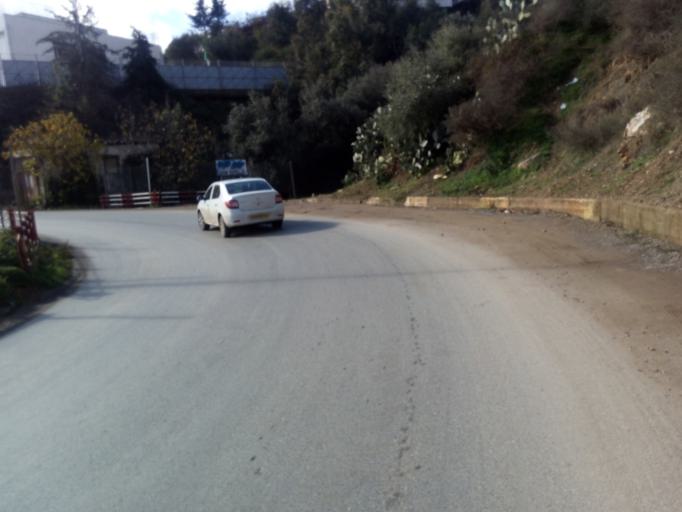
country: DZ
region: Tizi Ouzou
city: Chemini
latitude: 36.6071
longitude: 4.6394
